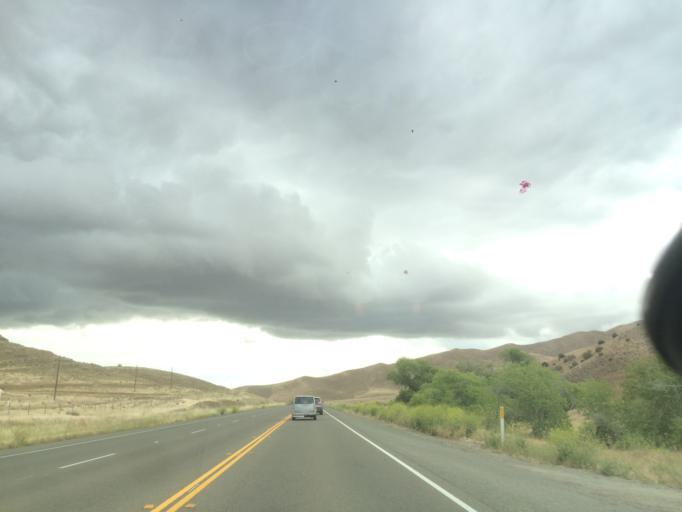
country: US
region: California
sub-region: Kings County
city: Avenal
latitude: 35.7749
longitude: -120.1494
